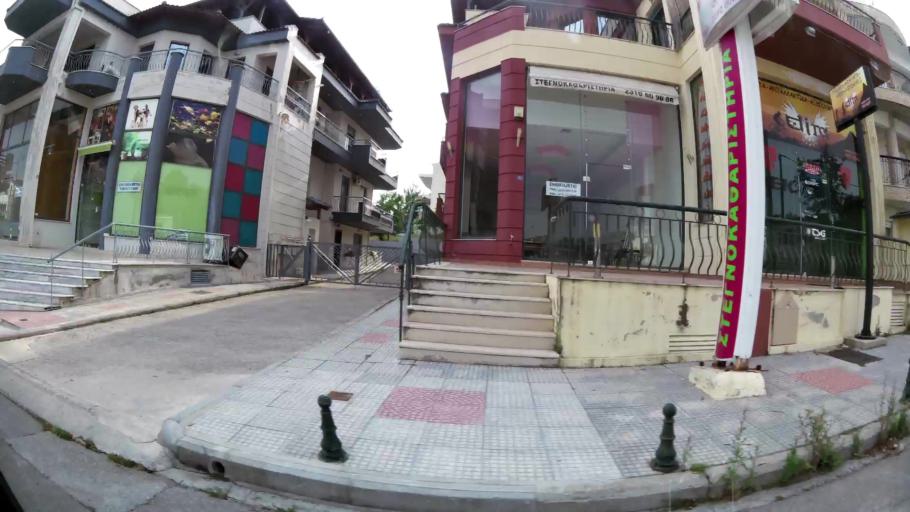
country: GR
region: Central Macedonia
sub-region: Nomos Thessalonikis
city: Oraiokastro
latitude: 40.7294
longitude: 22.9204
